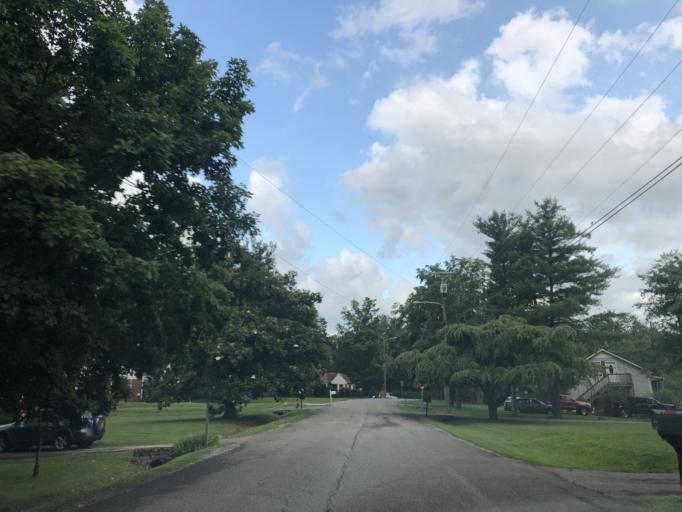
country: US
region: Tennessee
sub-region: Davidson County
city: Lakewood
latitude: 36.1782
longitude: -86.6876
